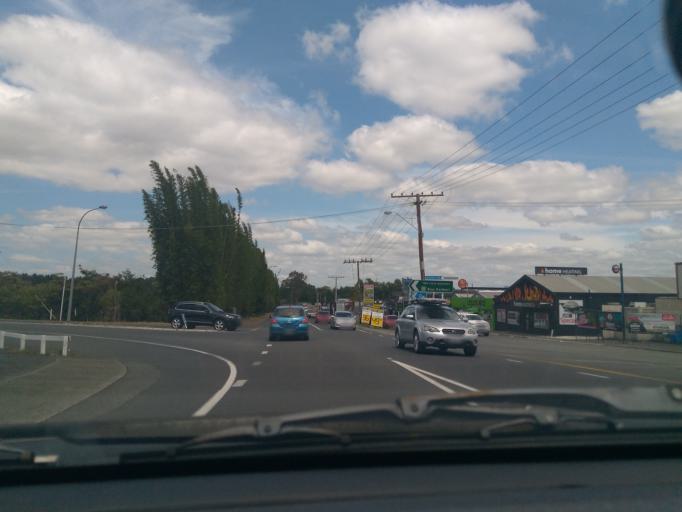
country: NZ
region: Northland
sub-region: Far North District
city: Kerikeri
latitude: -35.2063
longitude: 173.9174
